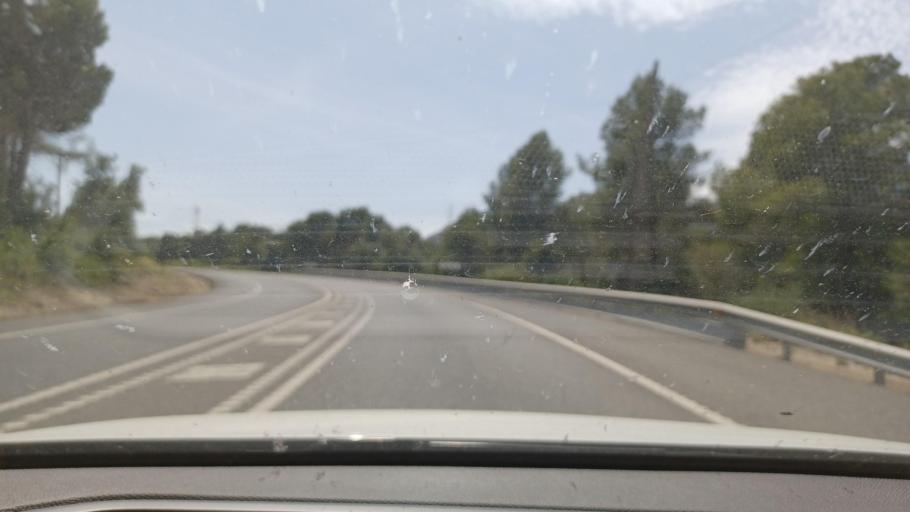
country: ES
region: Catalonia
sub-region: Provincia de Tarragona
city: l'Ametlla de Mar
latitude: 40.9762
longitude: 0.8848
